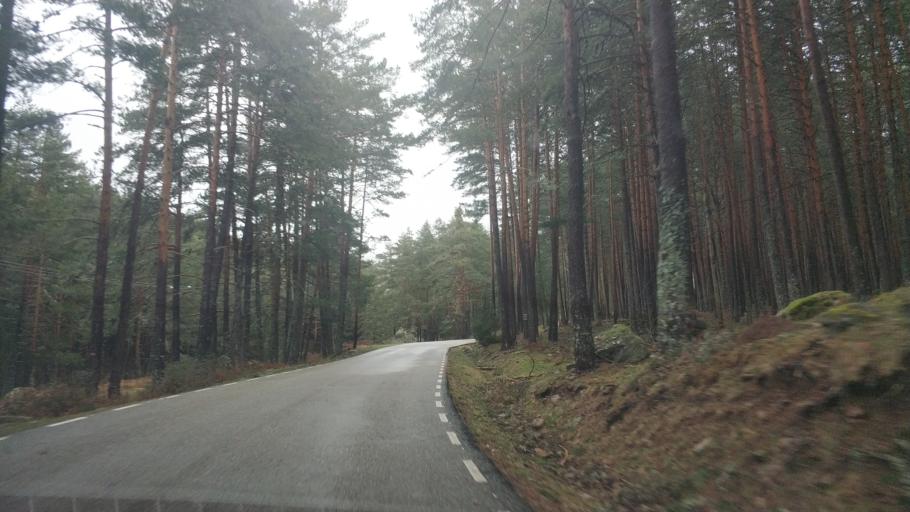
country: ES
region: Castille and Leon
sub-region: Provincia de Burgos
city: Neila
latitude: 42.0291
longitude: -3.0092
